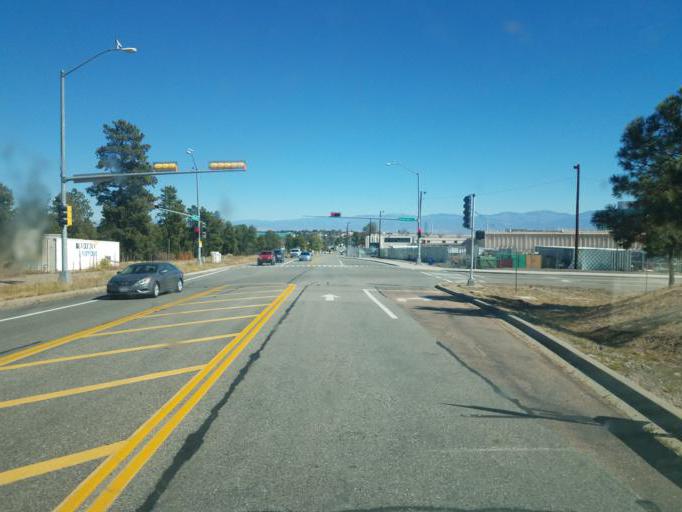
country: US
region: New Mexico
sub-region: Los Alamos County
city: Los Alamos
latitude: 35.8759
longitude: -106.3293
